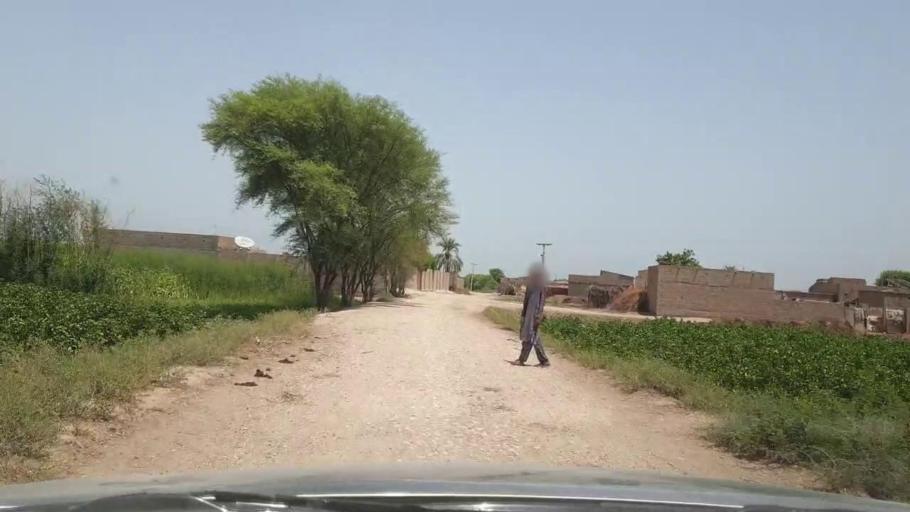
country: PK
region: Sindh
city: Pano Aqil
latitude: 27.8684
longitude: 69.1929
